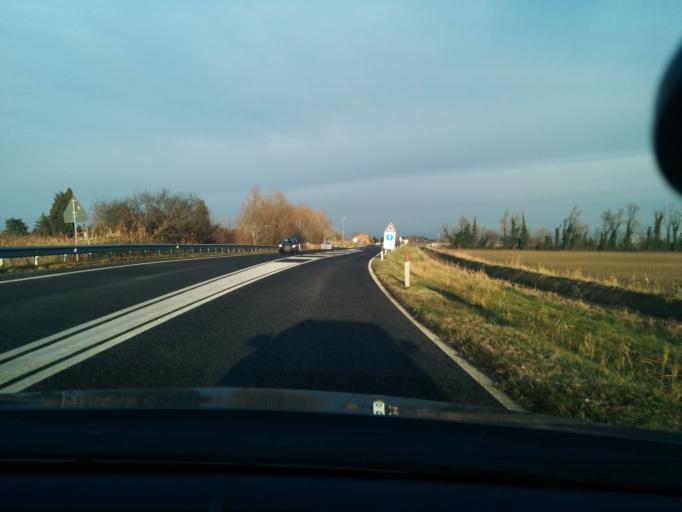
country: IT
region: Friuli Venezia Giulia
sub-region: Provincia di Gorizia
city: San Canzian d'Isonzo
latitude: 45.7451
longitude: 13.4466
